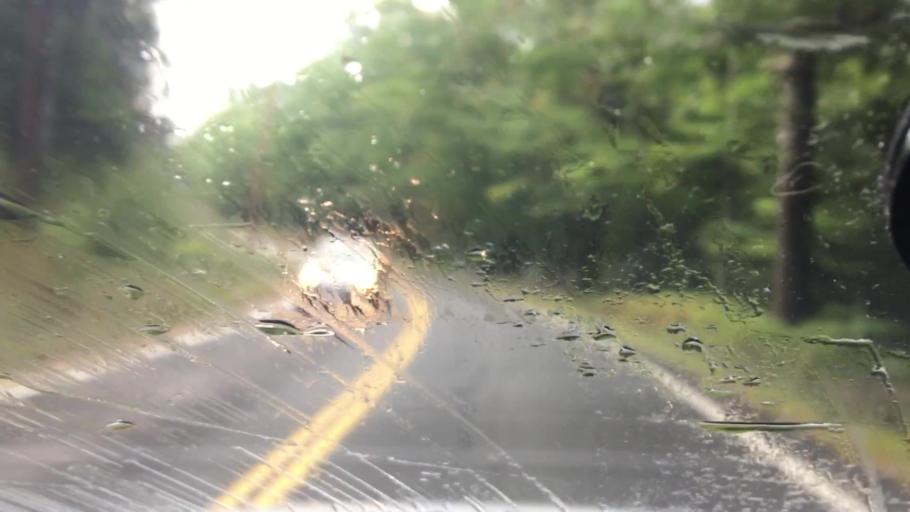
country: US
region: New Hampshire
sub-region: Carroll County
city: Wakefield
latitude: 43.6003
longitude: -71.0089
